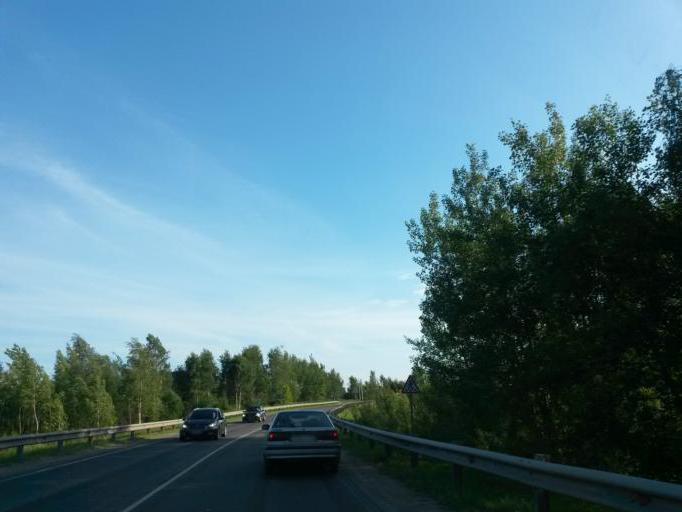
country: RU
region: Moskovskaya
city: Gorki-Leninskiye
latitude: 55.4856
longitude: 37.7801
